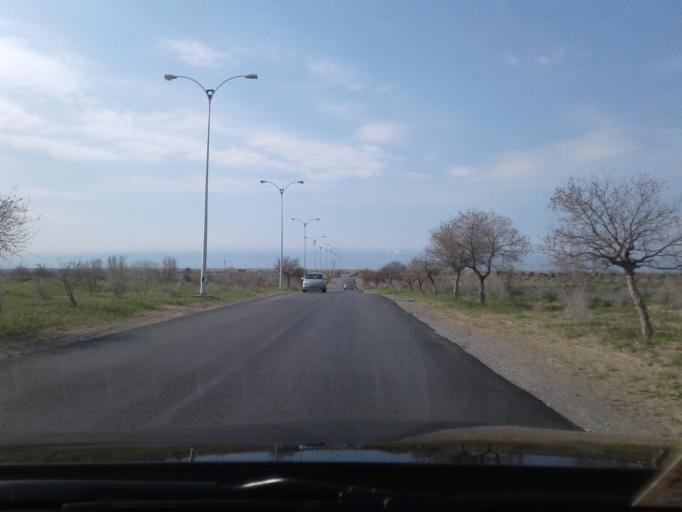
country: TM
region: Ahal
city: Ashgabat
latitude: 38.0933
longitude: 58.3835
